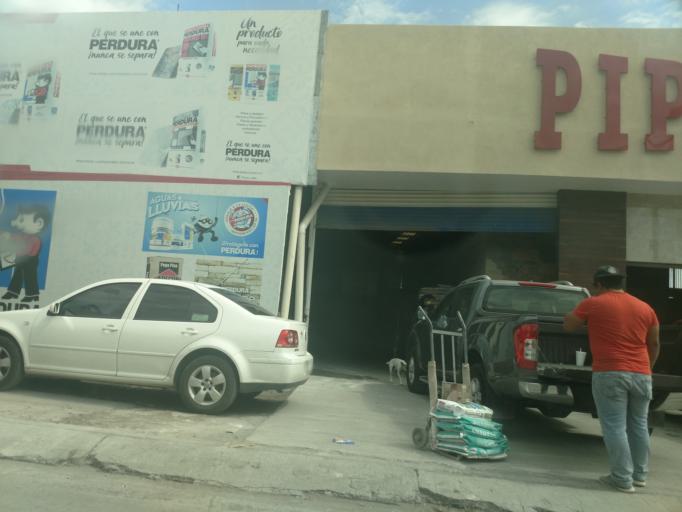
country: MX
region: Nayarit
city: Tepic
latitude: 21.4932
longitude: -104.8791
